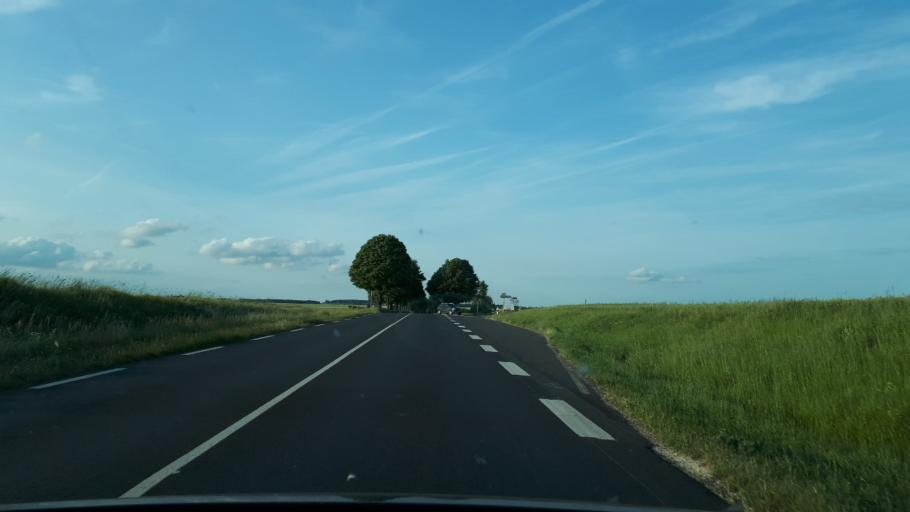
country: FR
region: Centre
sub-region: Departement du Loir-et-Cher
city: Naveil
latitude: 47.7385
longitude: 1.0334
